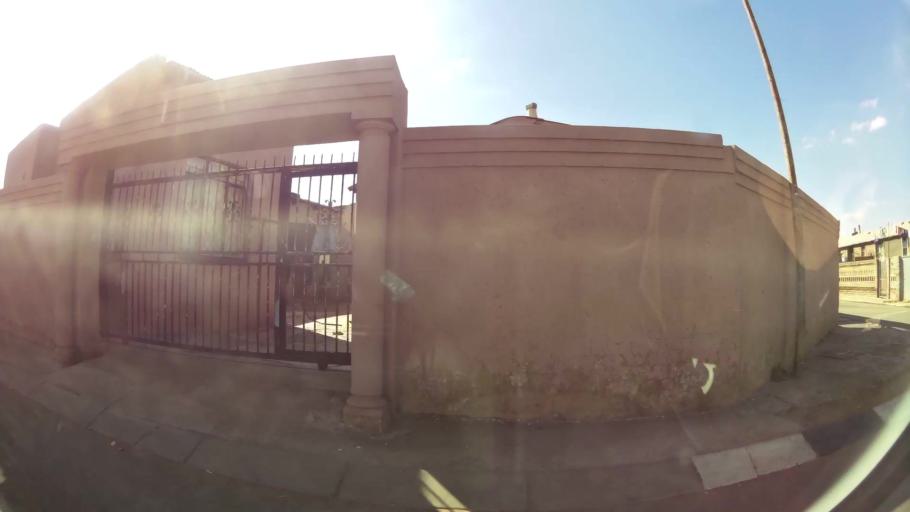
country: ZA
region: Gauteng
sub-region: City of Johannesburg Metropolitan Municipality
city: Soweto
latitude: -26.2238
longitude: 27.8946
